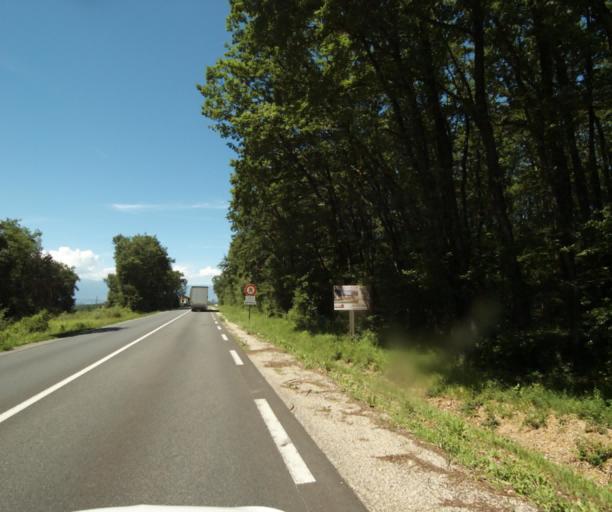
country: FR
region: Rhone-Alpes
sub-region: Departement de la Haute-Savoie
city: Loisin
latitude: 46.2651
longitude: 6.3169
